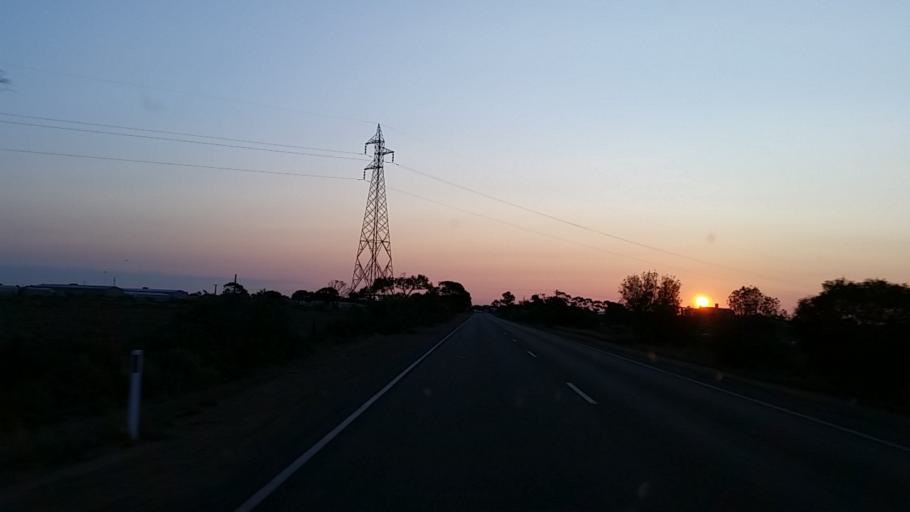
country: AU
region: South Australia
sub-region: Port Pirie City and Dists
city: Solomontown
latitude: -33.1811
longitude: 138.0386
